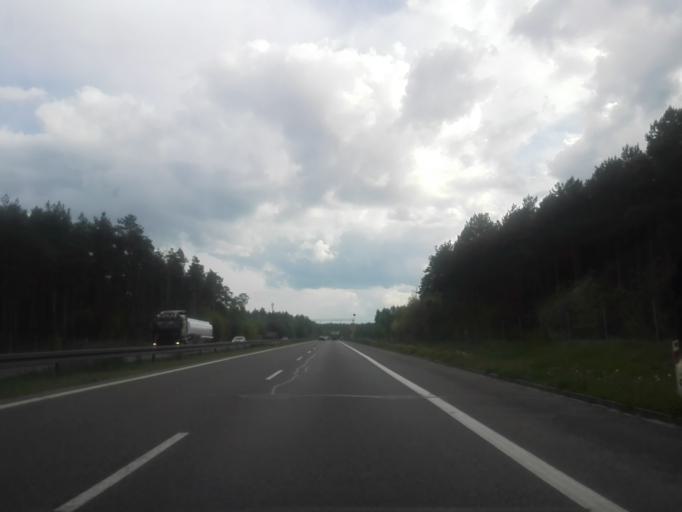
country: PL
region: Masovian Voivodeship
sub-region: Powiat ostrowski
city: Ostrow Mazowiecka
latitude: 52.7954
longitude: 21.8679
